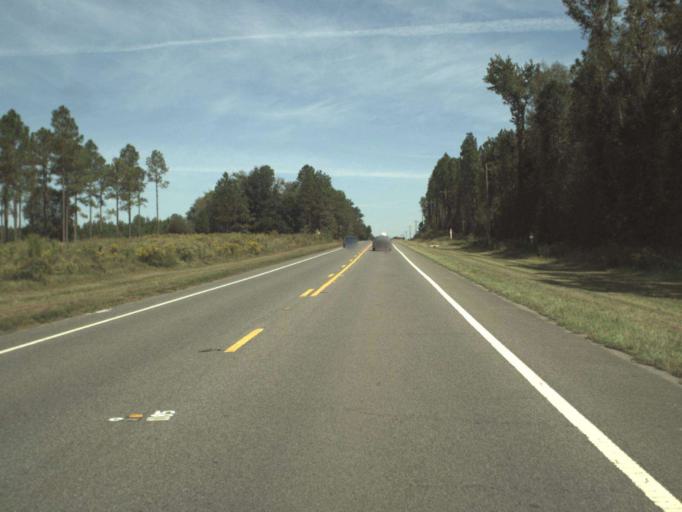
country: US
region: Florida
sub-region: Washington County
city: Chipley
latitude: 30.7112
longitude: -85.5582
